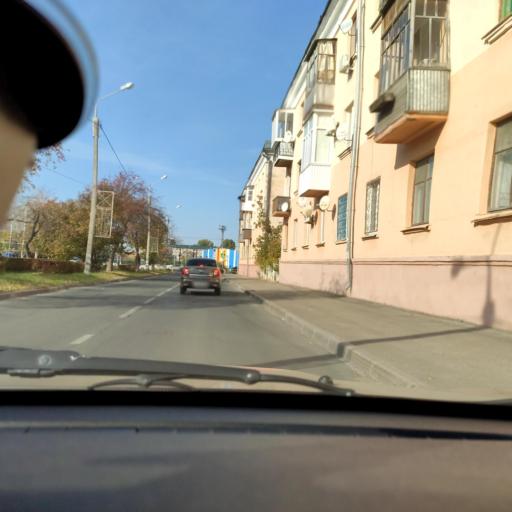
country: RU
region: Samara
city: Tol'yatti
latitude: 53.5119
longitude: 49.4100
